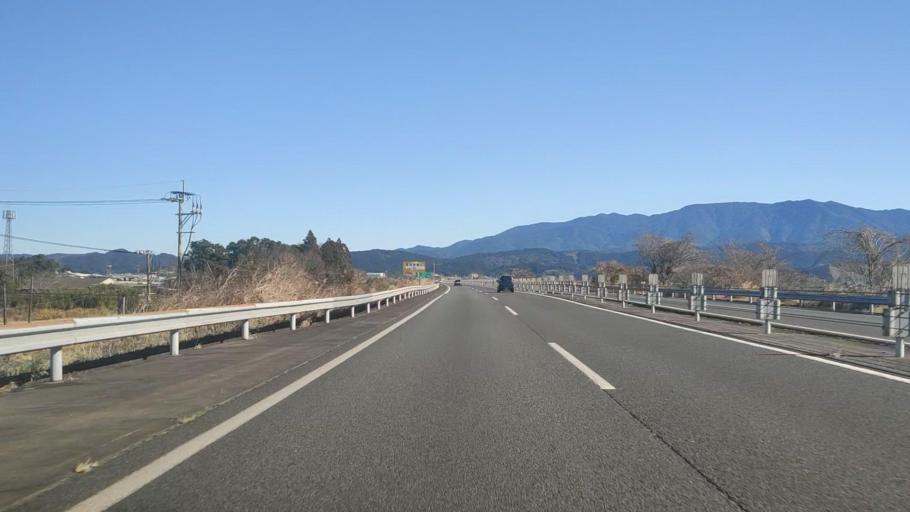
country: JP
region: Miyazaki
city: Miyakonojo
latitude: 31.7823
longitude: 131.1330
